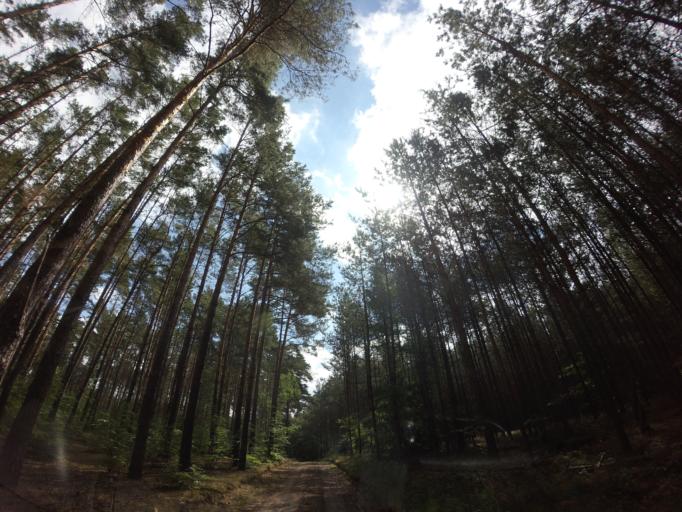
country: PL
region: West Pomeranian Voivodeship
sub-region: Powiat choszczenski
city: Bierzwnik
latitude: 53.0093
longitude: 15.7018
